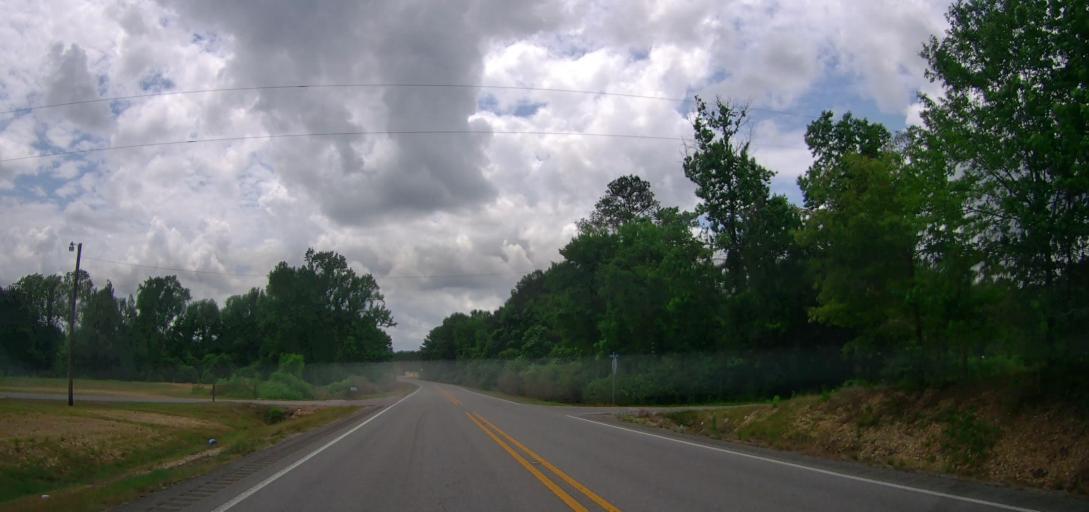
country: US
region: Alabama
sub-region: Marion County
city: Hamilton
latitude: 34.1373
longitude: -88.0121
